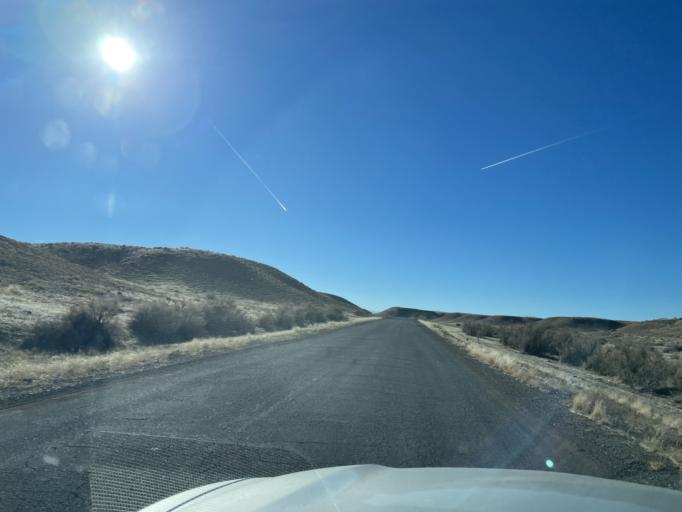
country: US
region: Colorado
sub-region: Mesa County
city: Loma
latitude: 39.2059
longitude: -109.1035
